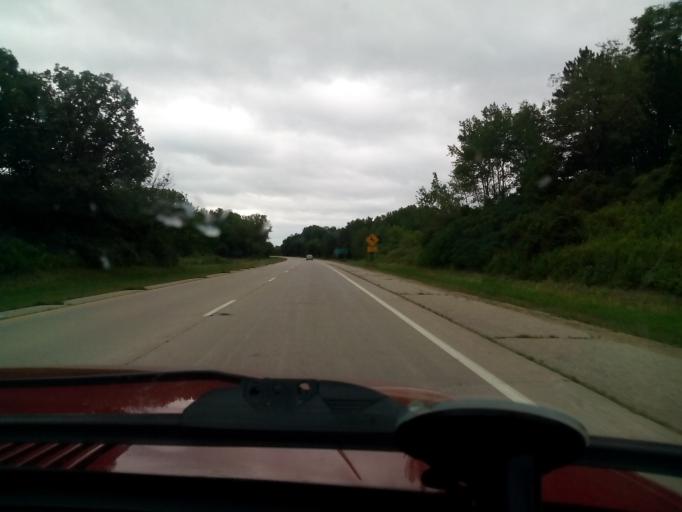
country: US
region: Wisconsin
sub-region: Dane County
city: Sun Prairie
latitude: 43.2319
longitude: -89.1561
